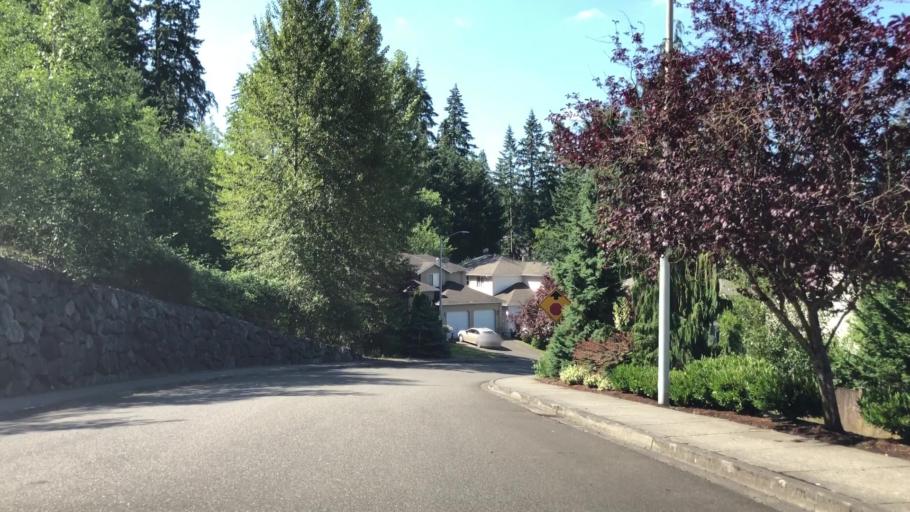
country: US
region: Washington
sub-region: Snohomish County
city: Alderwood Manor
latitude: 47.8181
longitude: -122.2502
